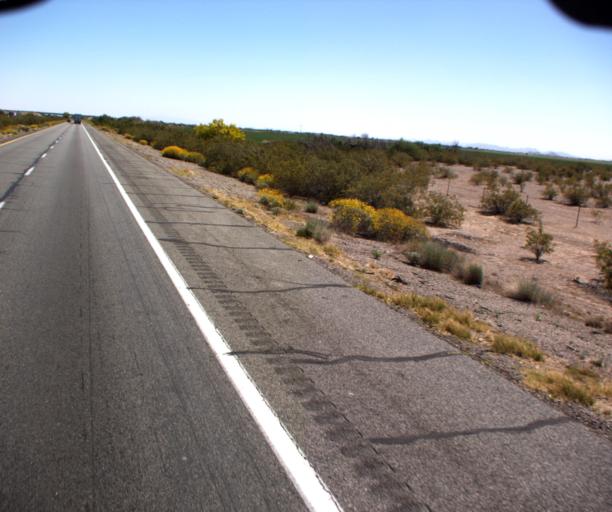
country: US
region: Arizona
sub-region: Maricopa County
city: Buckeye
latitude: 33.4918
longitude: -112.9126
